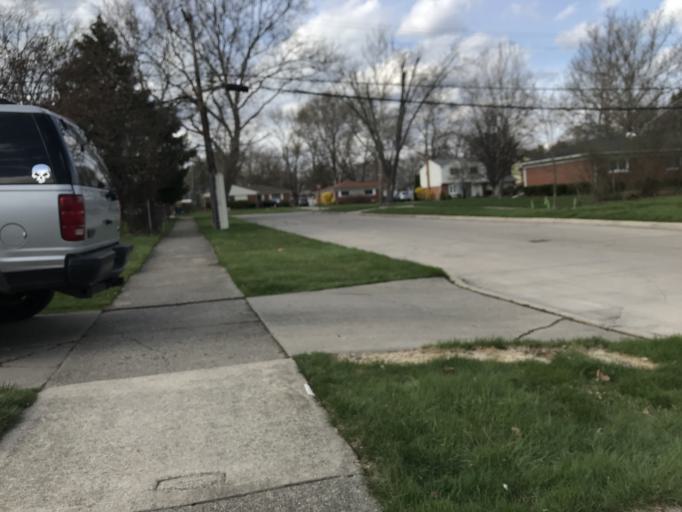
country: US
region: Michigan
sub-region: Oakland County
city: Farmington
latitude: 42.4626
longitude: -83.3451
